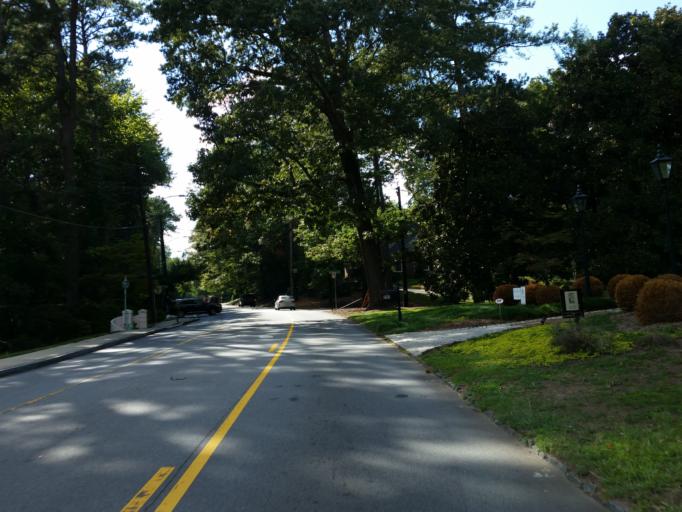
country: US
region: Georgia
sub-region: DeKalb County
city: North Atlanta
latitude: 33.8444
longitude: -84.3907
